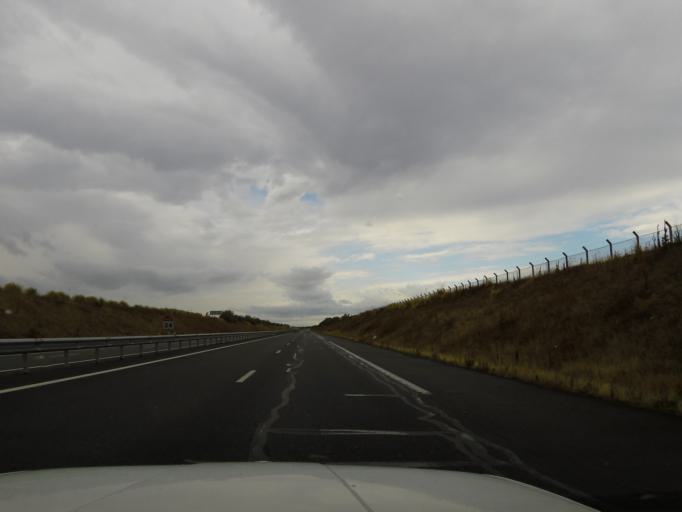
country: FR
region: Rhone-Alpes
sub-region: Departement de l'Isere
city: Janneyrias
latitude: 45.7379
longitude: 5.0956
